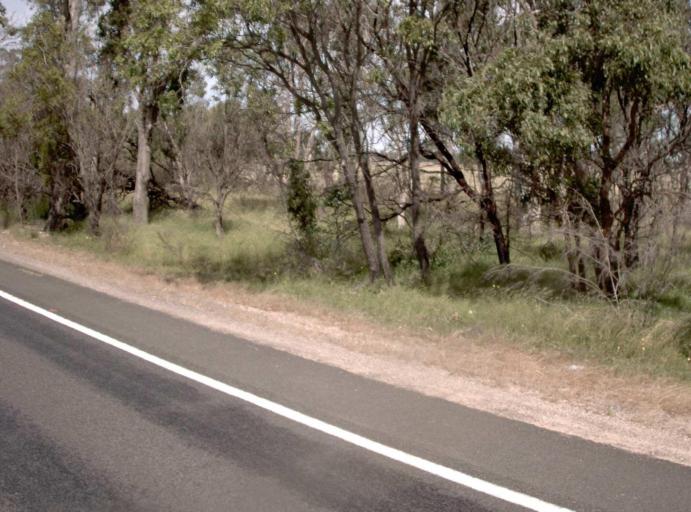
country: AU
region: Victoria
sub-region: East Gippsland
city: Bairnsdale
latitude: -37.8650
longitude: 147.4953
